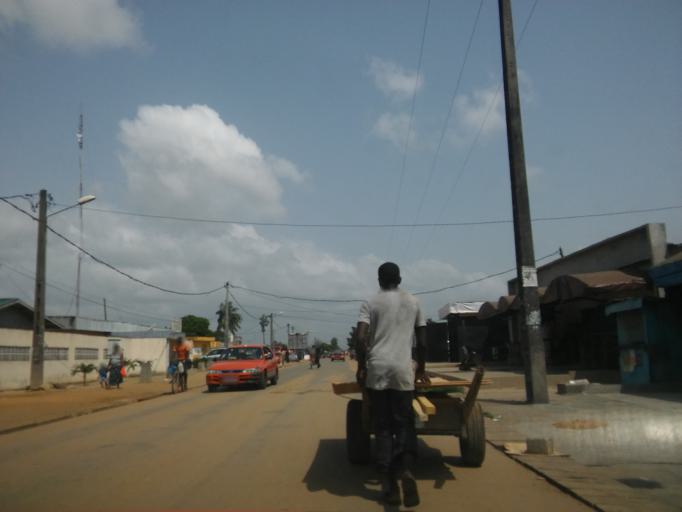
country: CI
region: Sud-Comoe
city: Grand-Bassam
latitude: 5.2123
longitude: -3.7374
